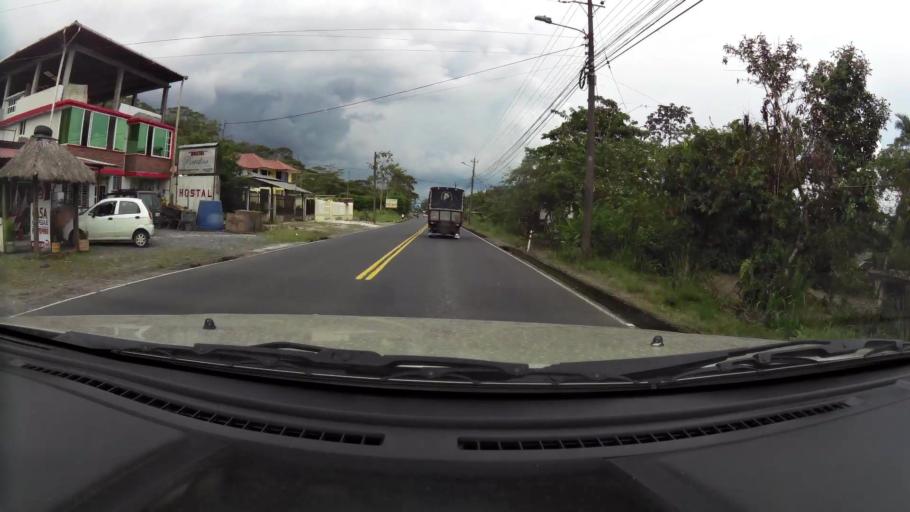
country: EC
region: Pastaza
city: Puyo
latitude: -1.5041
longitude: -78.0251
